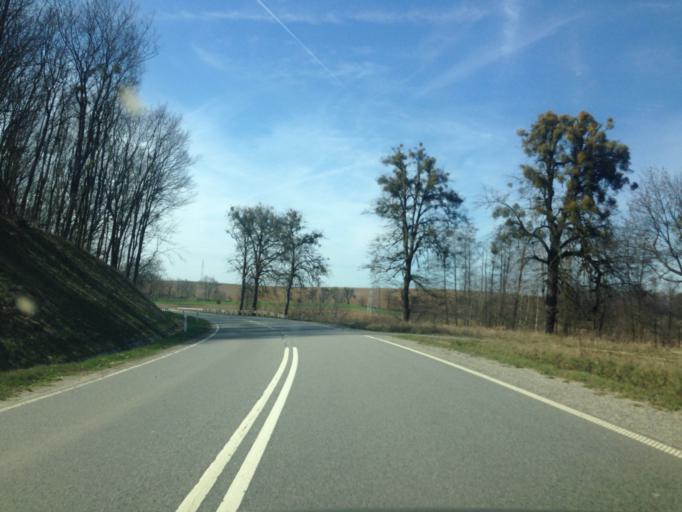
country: PL
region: Pomeranian Voivodeship
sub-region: Powiat starogardzki
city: Smetowo Graniczne
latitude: 53.7384
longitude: 18.7105
